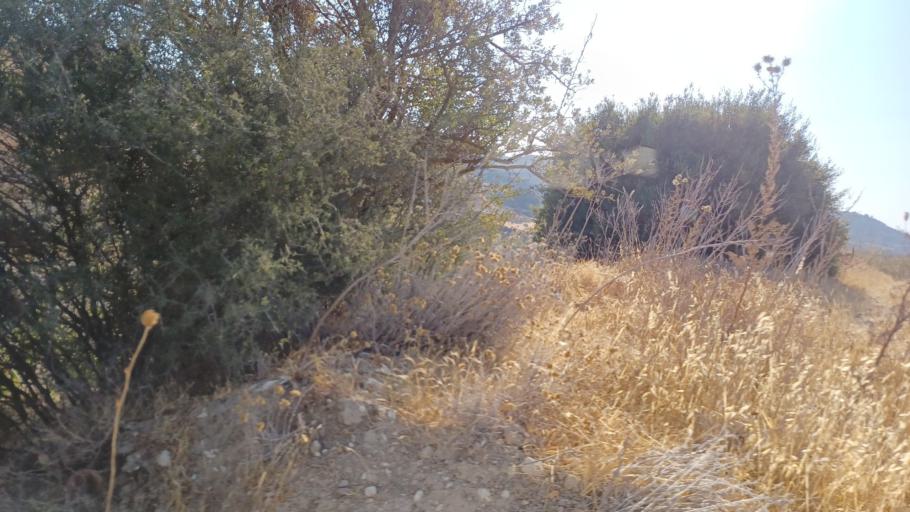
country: CY
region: Pafos
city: Tala
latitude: 34.9109
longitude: 32.4952
